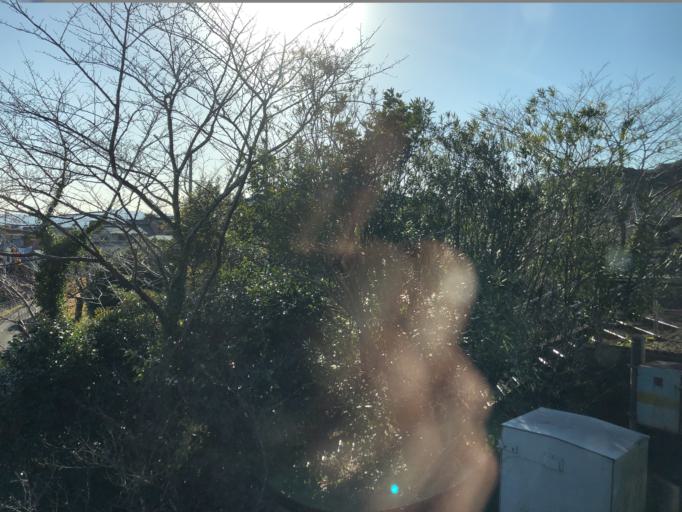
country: JP
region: Kochi
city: Nakamura
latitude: 33.0430
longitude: 133.0567
